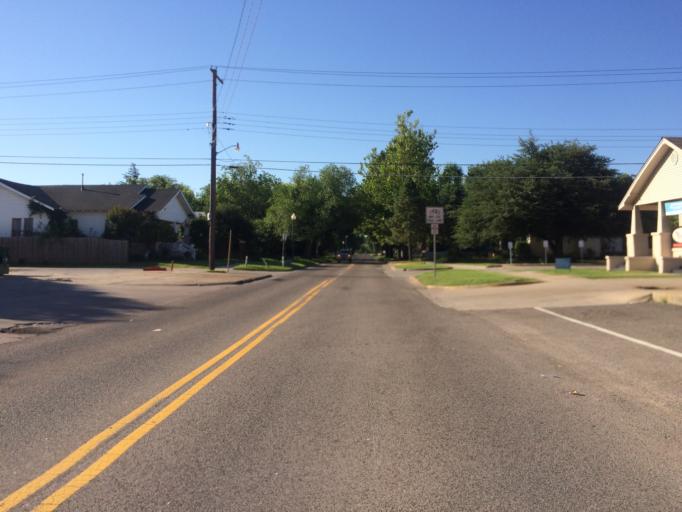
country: US
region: Oklahoma
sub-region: Cleveland County
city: Norman
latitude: 35.2188
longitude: -97.4480
